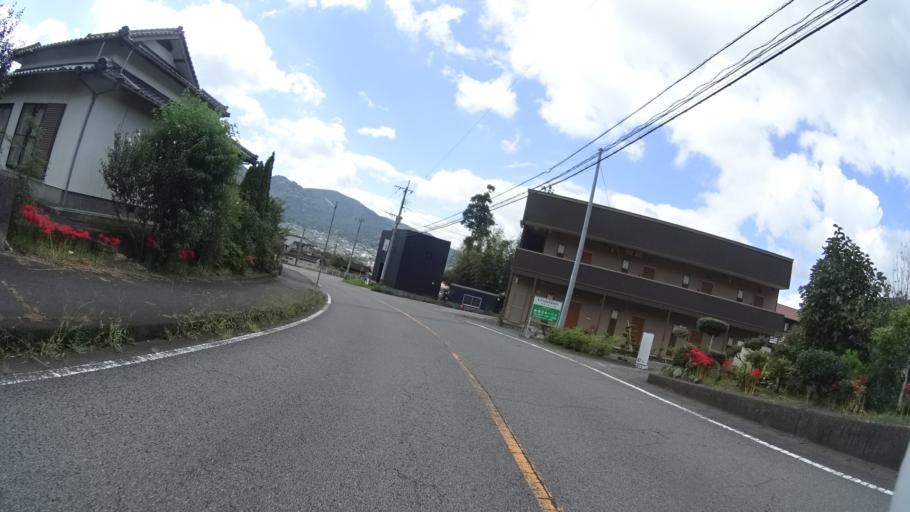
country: JP
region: Oita
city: Beppu
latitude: 33.2723
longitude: 131.3635
